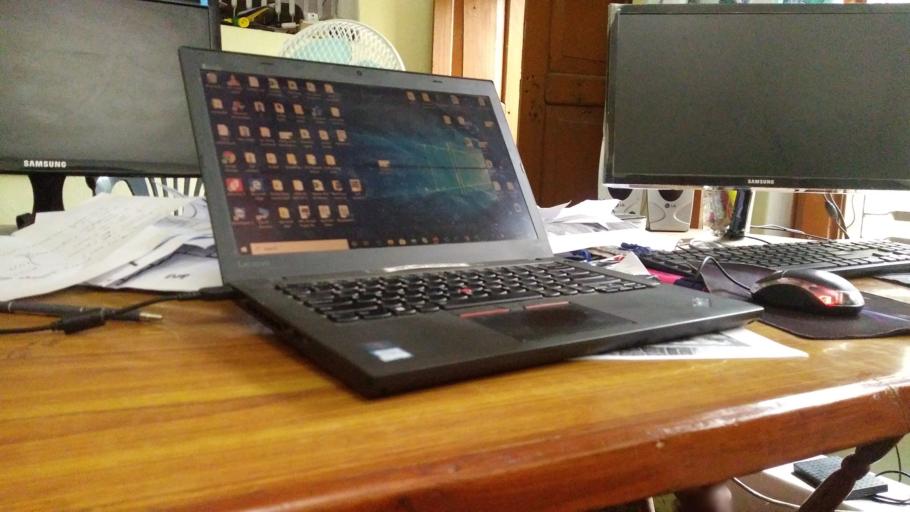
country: NP
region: Western Region
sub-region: Lumbini Zone
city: Bhairahawa
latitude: 27.5119
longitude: 83.4564
